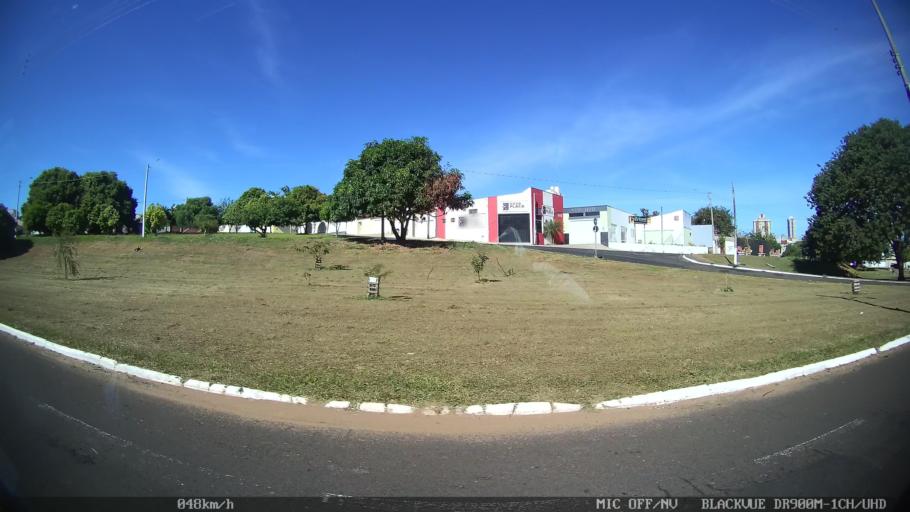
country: BR
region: Sao Paulo
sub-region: Franca
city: Franca
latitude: -20.5199
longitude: -47.3889
